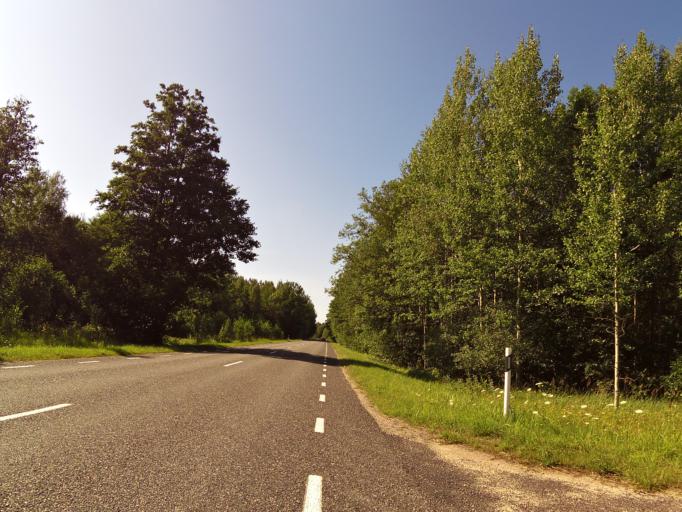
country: EE
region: Hiiumaa
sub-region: Kaerdla linn
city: Kardla
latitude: 58.7258
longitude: 22.5586
